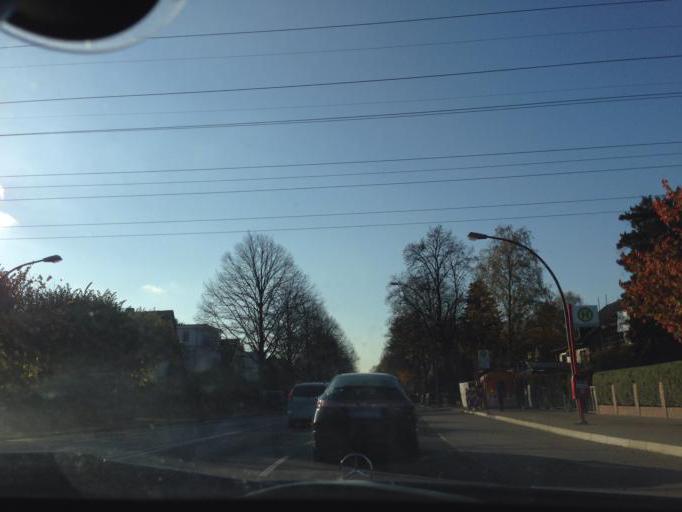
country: DE
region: Hamburg
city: Wandsbek
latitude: 53.5705
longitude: 10.1051
